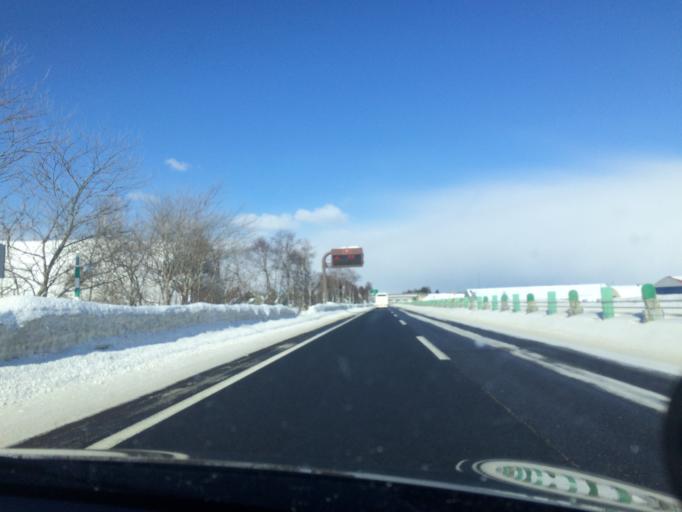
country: JP
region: Hokkaido
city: Chitose
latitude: 42.8651
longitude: 141.5570
